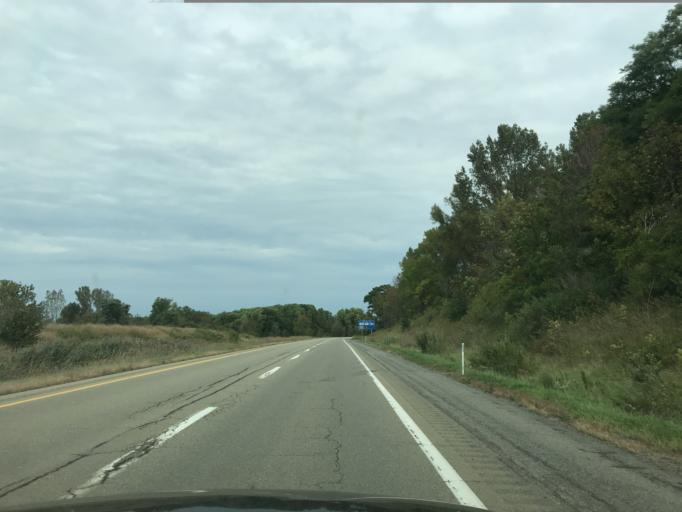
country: US
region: Pennsylvania
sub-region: Erie County
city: Erie
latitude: 42.0539
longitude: -80.1127
